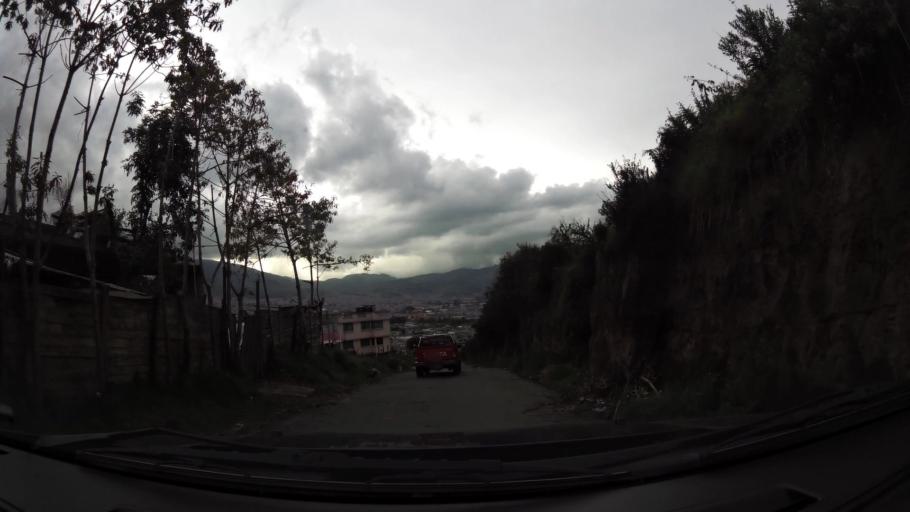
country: EC
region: Pichincha
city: Sangolqui
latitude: -0.3175
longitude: -78.5327
